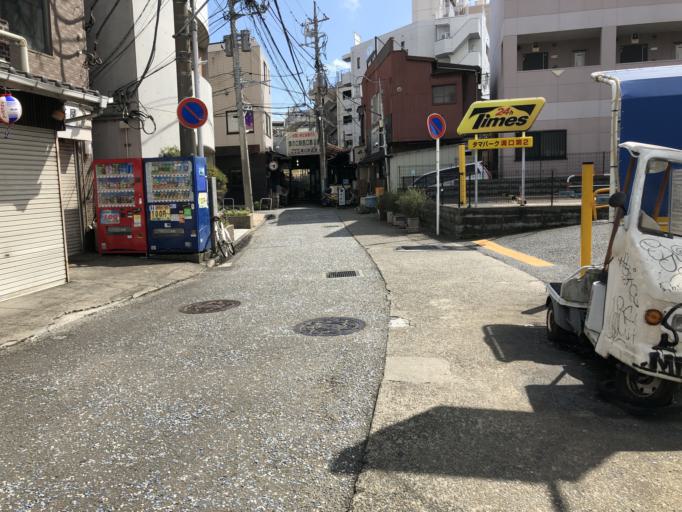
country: JP
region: Tokyo
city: Chofugaoka
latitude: 35.6006
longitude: 139.6094
